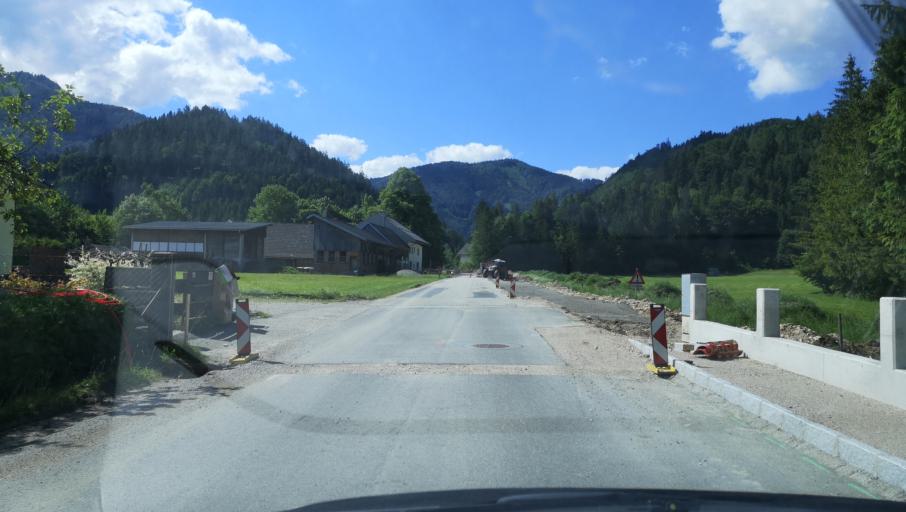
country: AT
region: Lower Austria
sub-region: Politischer Bezirk Scheibbs
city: Gresten
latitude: 47.9461
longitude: 15.0284
